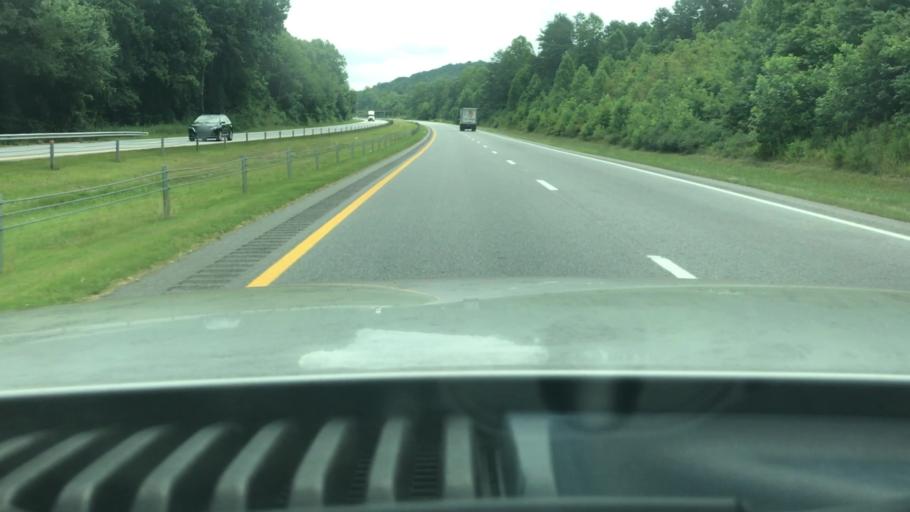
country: US
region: North Carolina
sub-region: Wilkes County
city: North Wilkesboro
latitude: 36.1394
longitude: -81.0780
